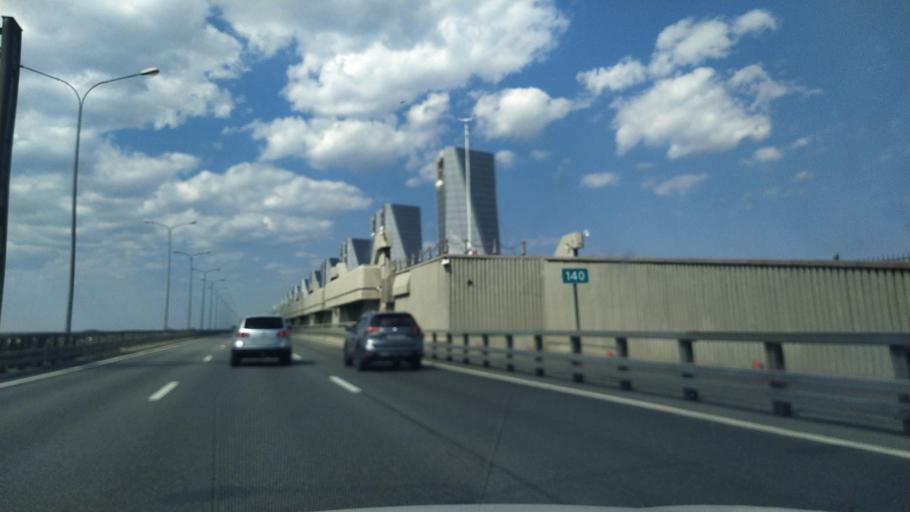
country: RU
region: Leningrad
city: Gorskaya
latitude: 60.0372
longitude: 29.9567
